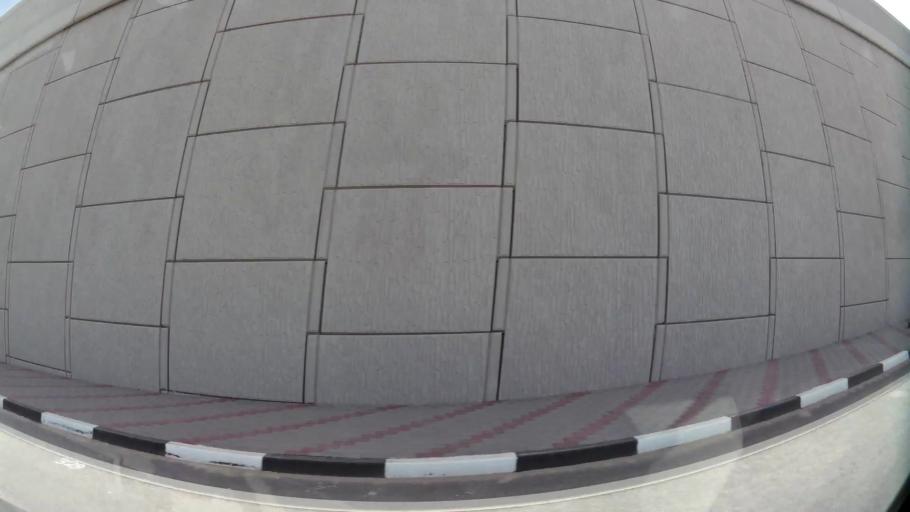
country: QA
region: Baladiyat Umm Salal
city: Umm Salal Muhammad
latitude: 25.3658
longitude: 51.4498
